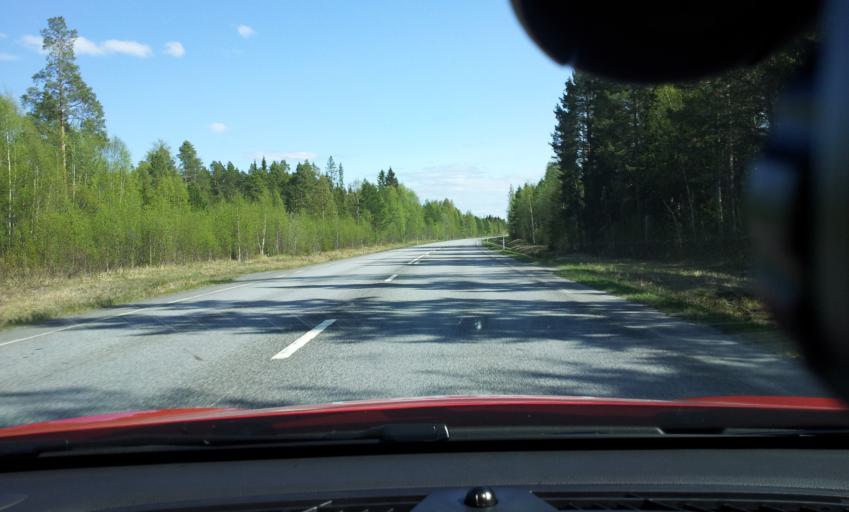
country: SE
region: Jaemtland
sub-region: Krokoms Kommun
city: Valla
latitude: 63.3327
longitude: 14.0274
